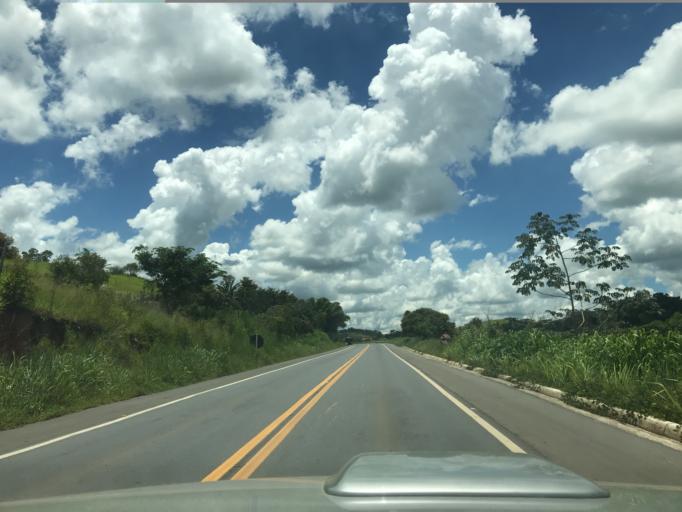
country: BR
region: Minas Gerais
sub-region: Perdoes
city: Perdoes
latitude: -21.0924
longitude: -45.0999
